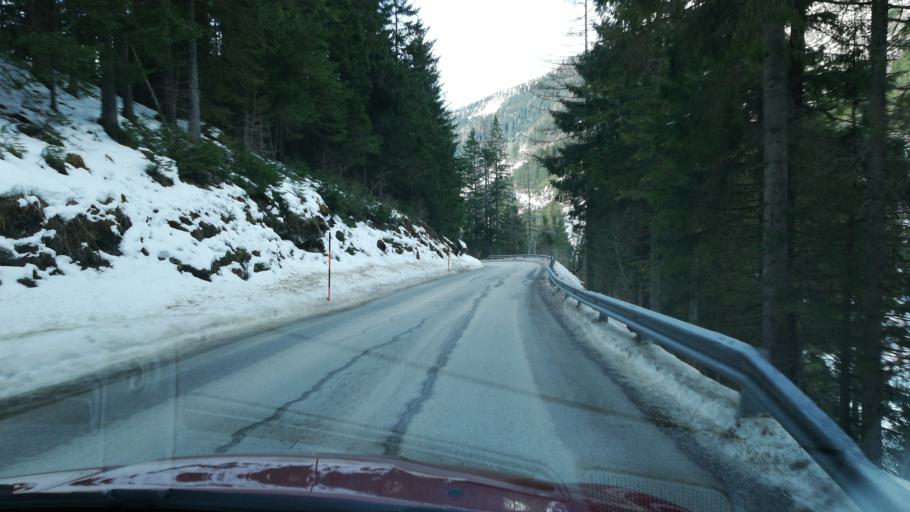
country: AT
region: Styria
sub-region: Politischer Bezirk Liezen
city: Donnersbach
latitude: 47.4188
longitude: 14.1706
